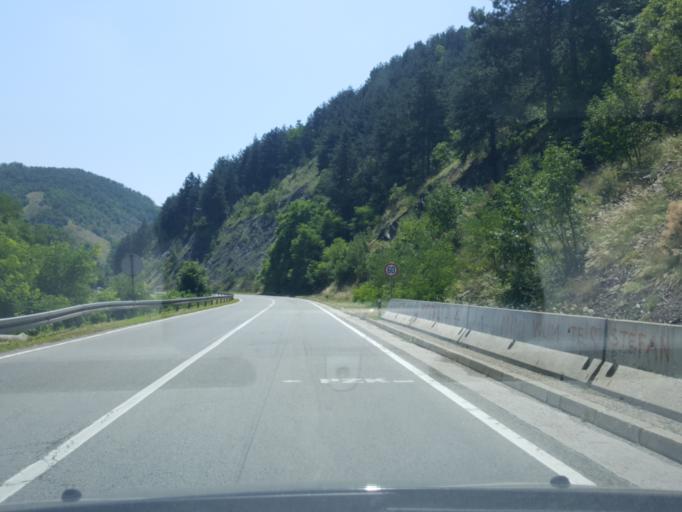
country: RS
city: Prislonica
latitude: 43.9866
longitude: 20.4182
